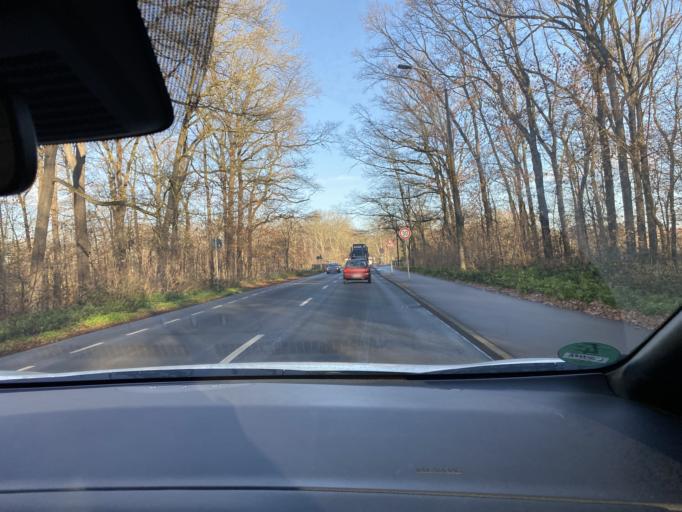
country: DE
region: Saxony
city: Leipzig
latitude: 51.3662
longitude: 12.3138
